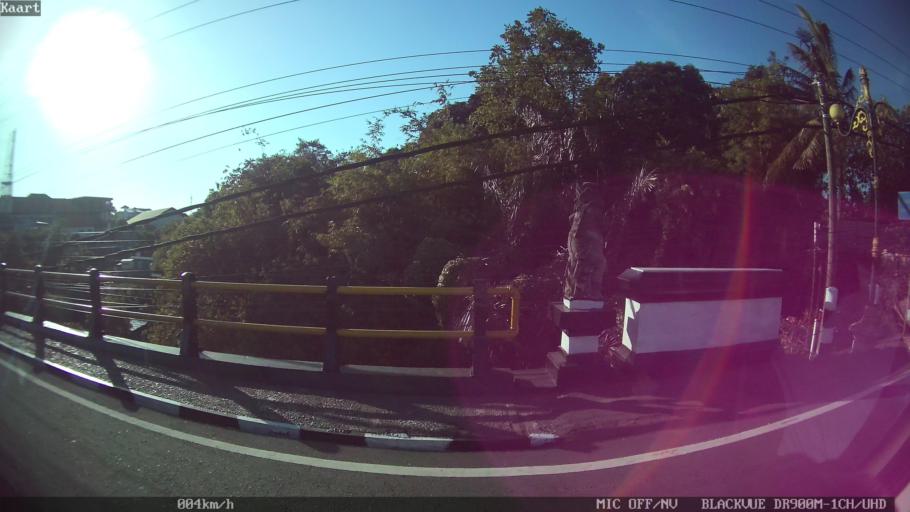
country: ID
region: Bali
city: Denpasar
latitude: -8.6383
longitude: 115.2101
